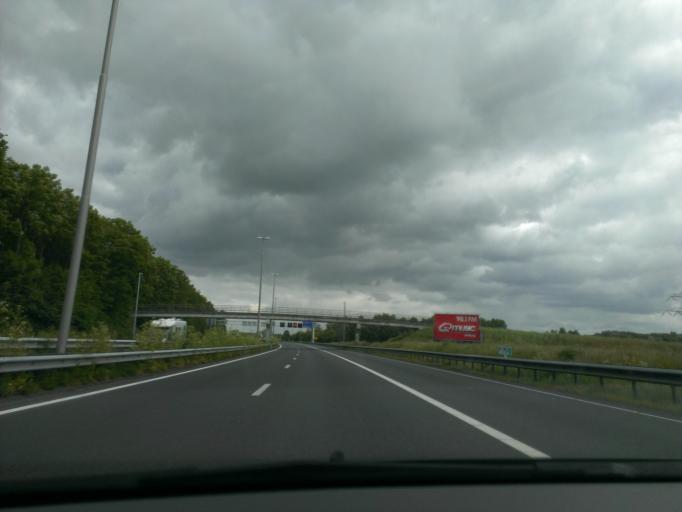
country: NL
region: Limburg
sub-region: Gemeente Sittard-Geleen
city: Born
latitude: 51.0321
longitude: 5.8229
